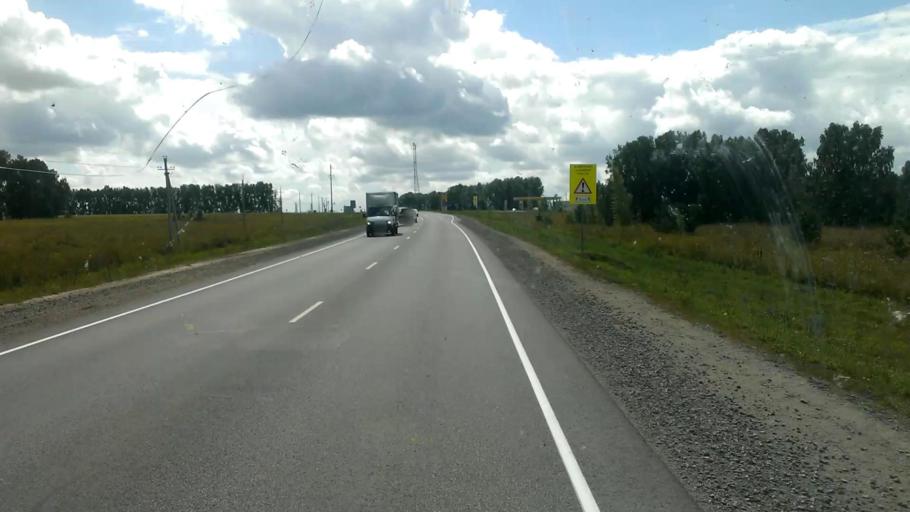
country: RU
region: Altai Krai
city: Troitskoye
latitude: 52.9711
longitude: 84.7484
